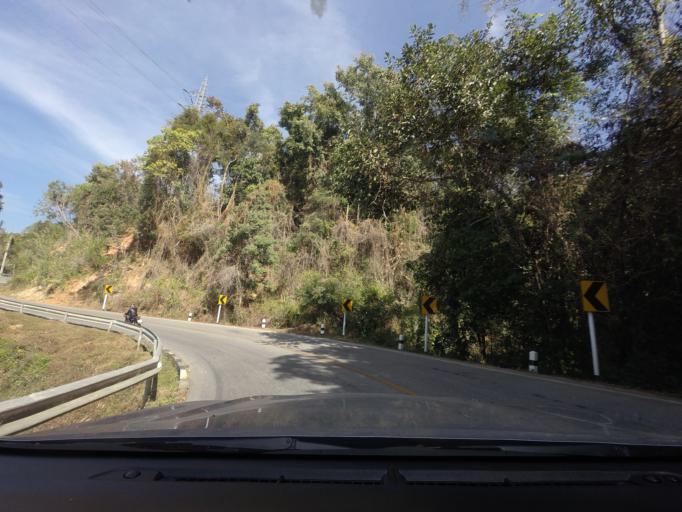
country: TH
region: Mae Hong Son
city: Mae Hi
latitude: 19.2702
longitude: 98.5409
